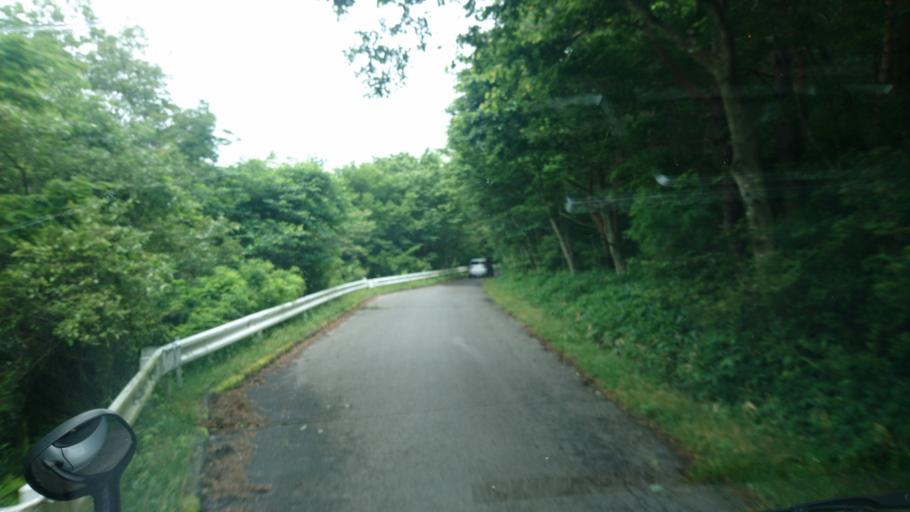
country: JP
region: Iwate
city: Ofunato
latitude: 39.1364
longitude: 141.7557
